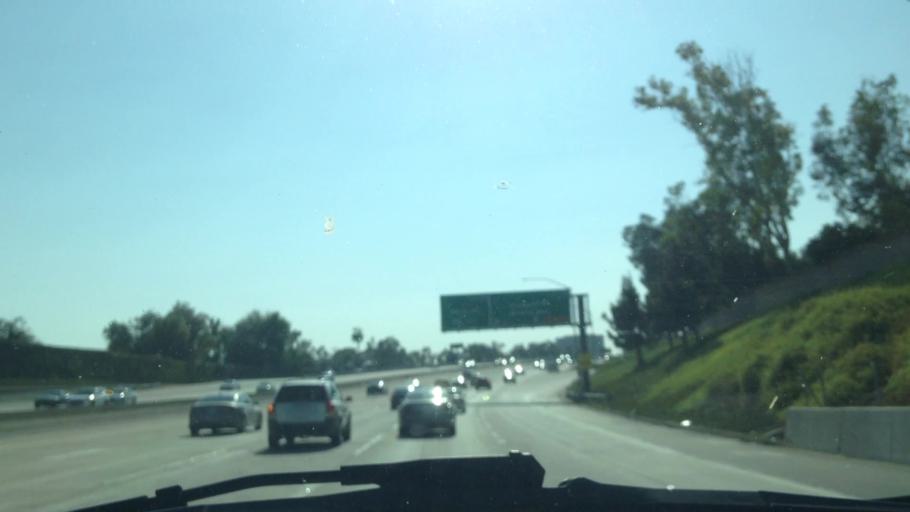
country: US
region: California
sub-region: Orange County
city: Orange
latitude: 33.7754
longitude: -117.8485
